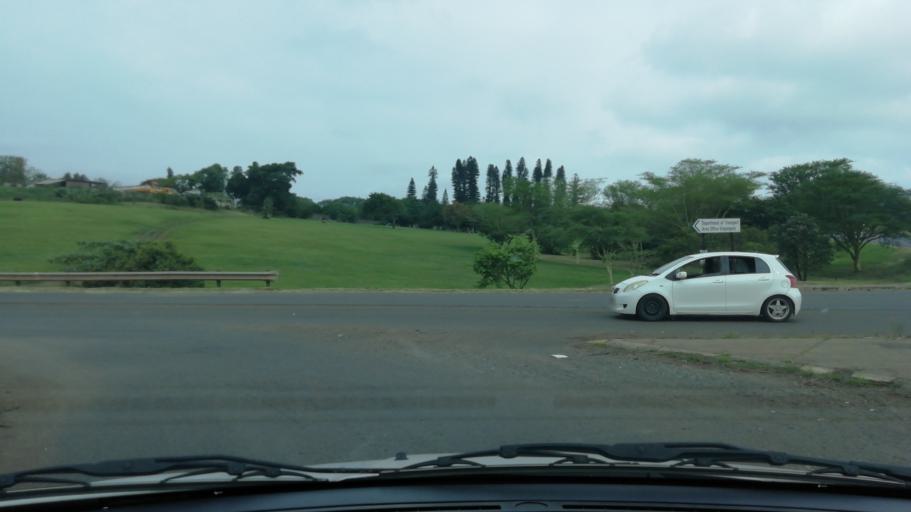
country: ZA
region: KwaZulu-Natal
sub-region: uThungulu District Municipality
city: Empangeni
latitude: -28.7415
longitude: 31.8822
